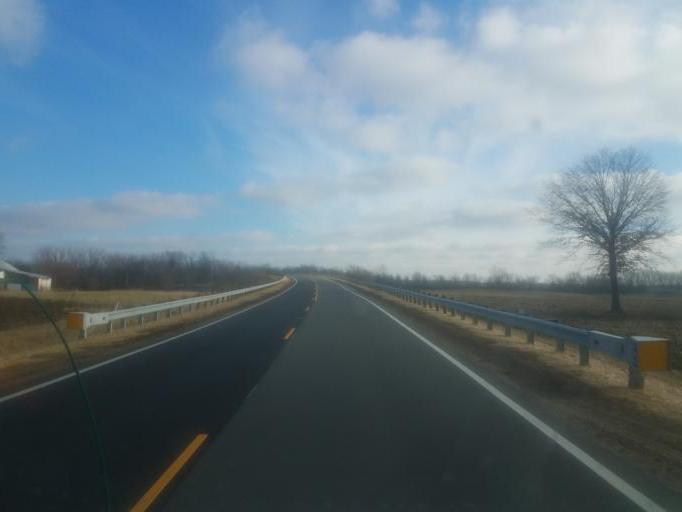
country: US
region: Ohio
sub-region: Morrow County
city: Mount Gilead
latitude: 40.6485
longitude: -82.9011
